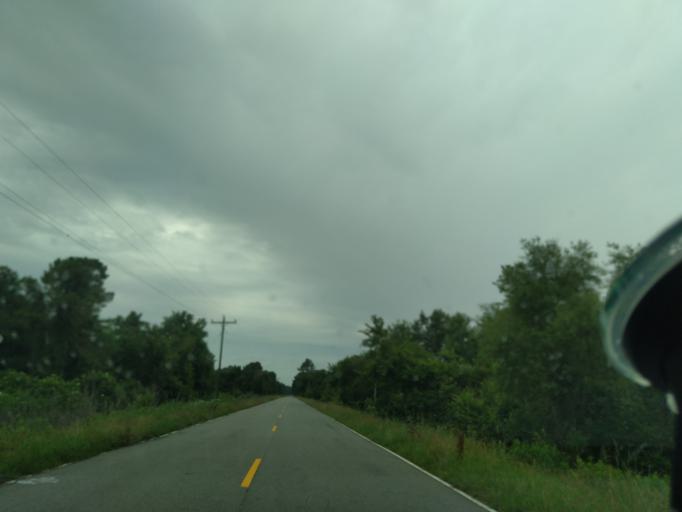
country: US
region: North Carolina
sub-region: Washington County
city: Plymouth
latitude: 35.8016
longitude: -76.5170
